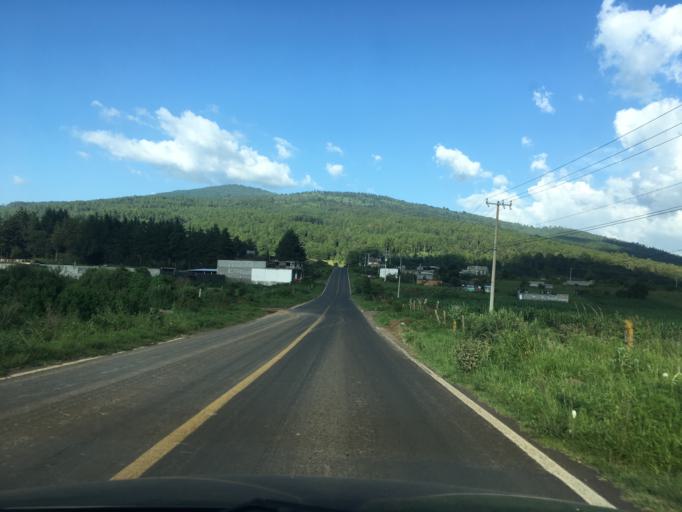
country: MX
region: Michoacan
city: Nahuatzen
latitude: 19.6468
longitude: -101.9131
